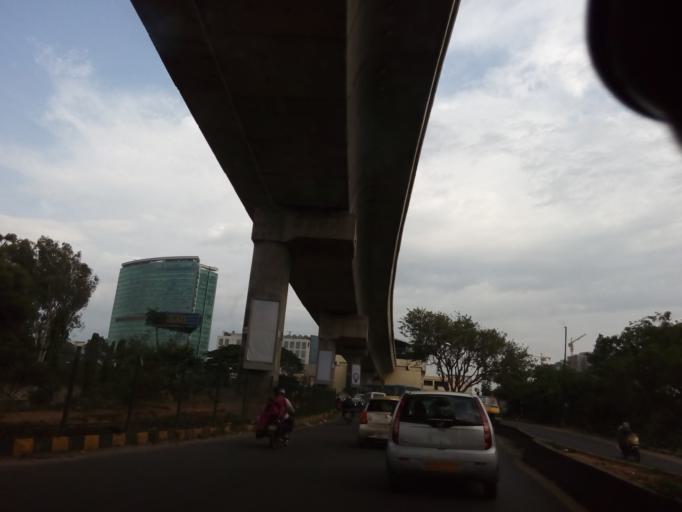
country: IN
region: Karnataka
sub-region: Bangalore Urban
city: Bangalore
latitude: 13.0166
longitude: 77.5538
